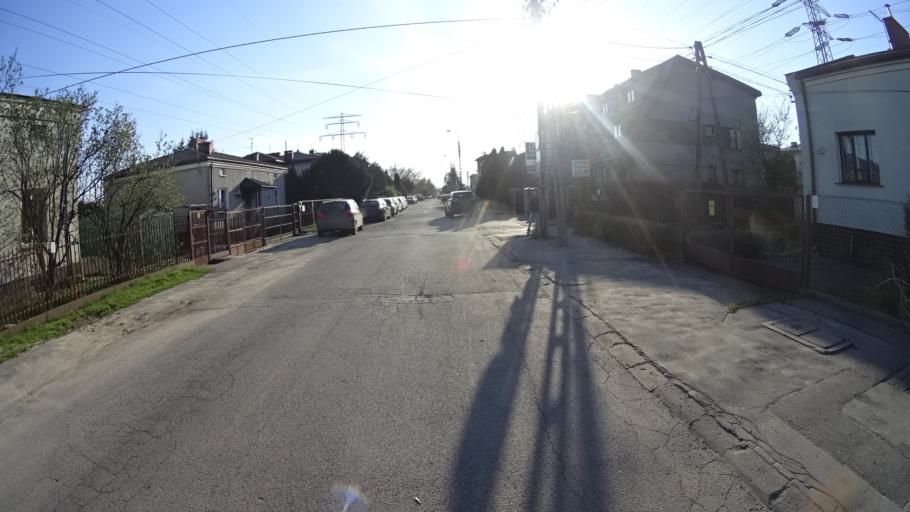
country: PL
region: Masovian Voivodeship
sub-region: Warszawa
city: Ursus
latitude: 52.2168
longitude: 20.9066
